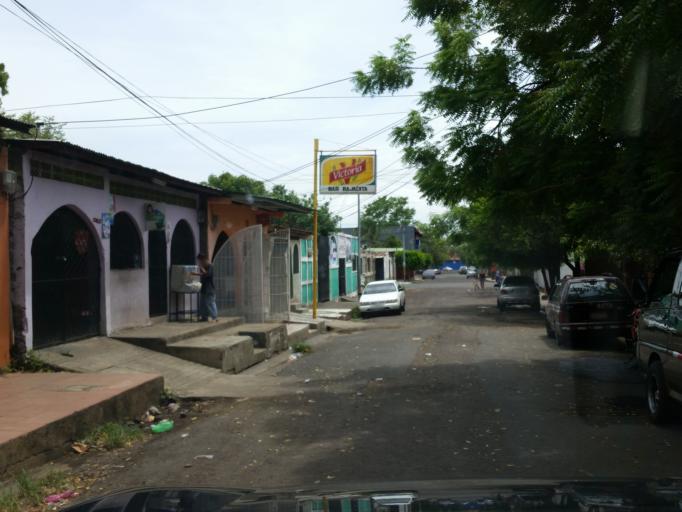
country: NI
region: Managua
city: Managua
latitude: 12.1449
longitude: -86.2673
